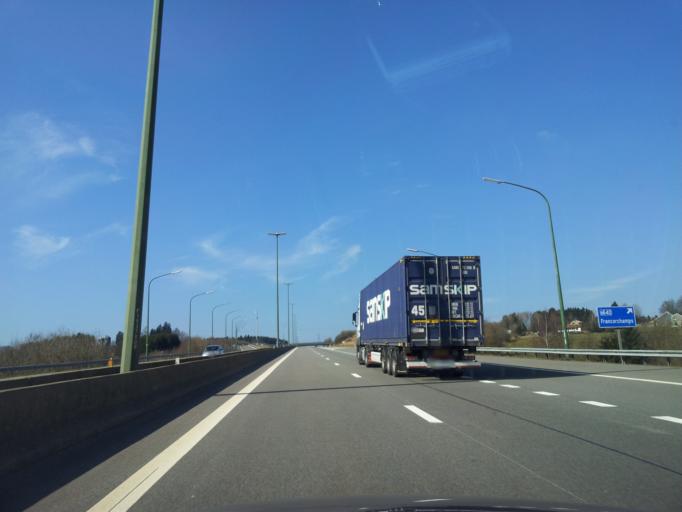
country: BE
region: Wallonia
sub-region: Province de Liege
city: Malmedy
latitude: 50.4753
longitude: 5.9723
